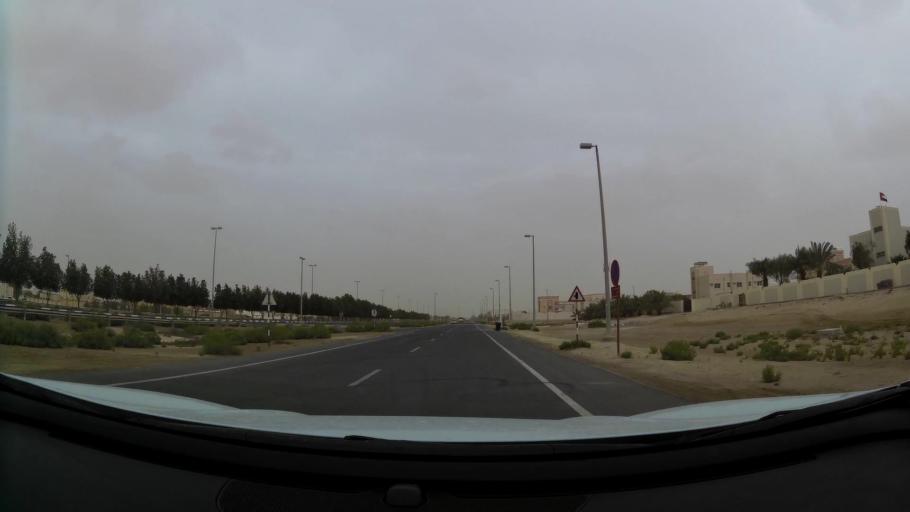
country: AE
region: Abu Dhabi
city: Abu Dhabi
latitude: 24.3811
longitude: 54.6966
